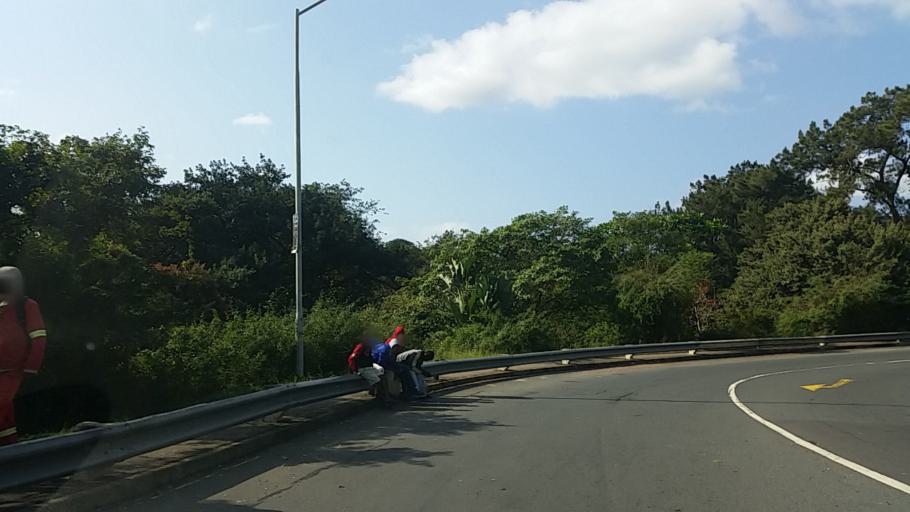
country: ZA
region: KwaZulu-Natal
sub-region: eThekwini Metropolitan Municipality
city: Berea
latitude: -29.8331
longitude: 30.9157
